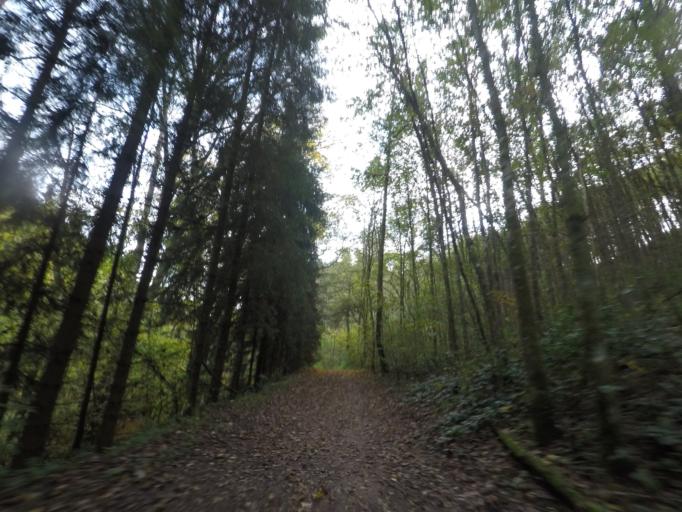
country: LU
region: Luxembourg
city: Itzig
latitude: 49.5990
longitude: 6.1602
